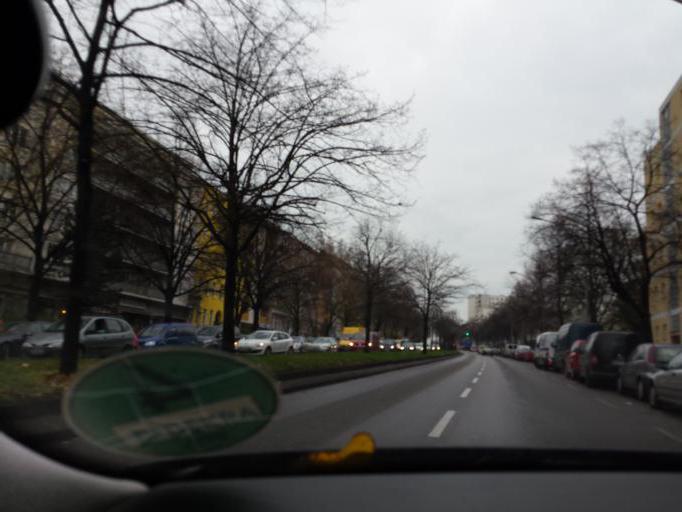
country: DE
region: Berlin
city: Bezirk Kreuzberg
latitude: 52.4891
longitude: 13.3861
